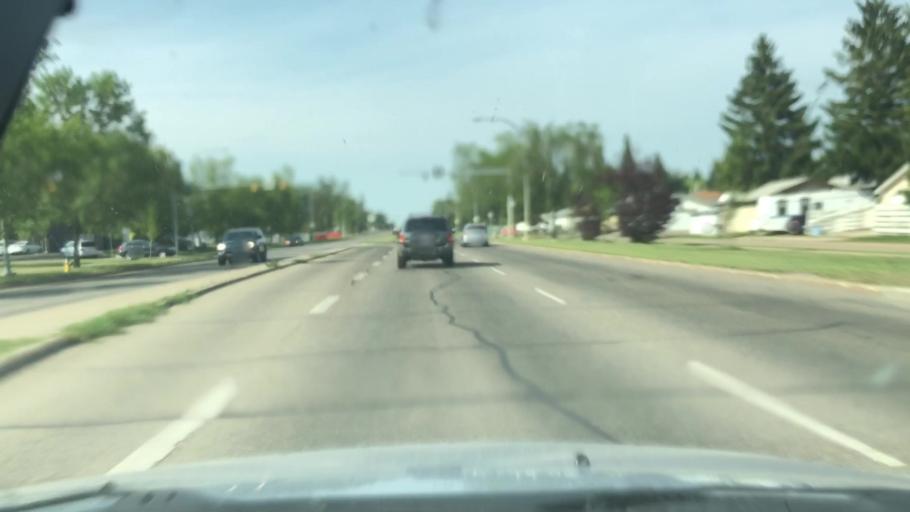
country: CA
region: Alberta
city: Edmonton
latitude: 53.6058
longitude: -113.4428
